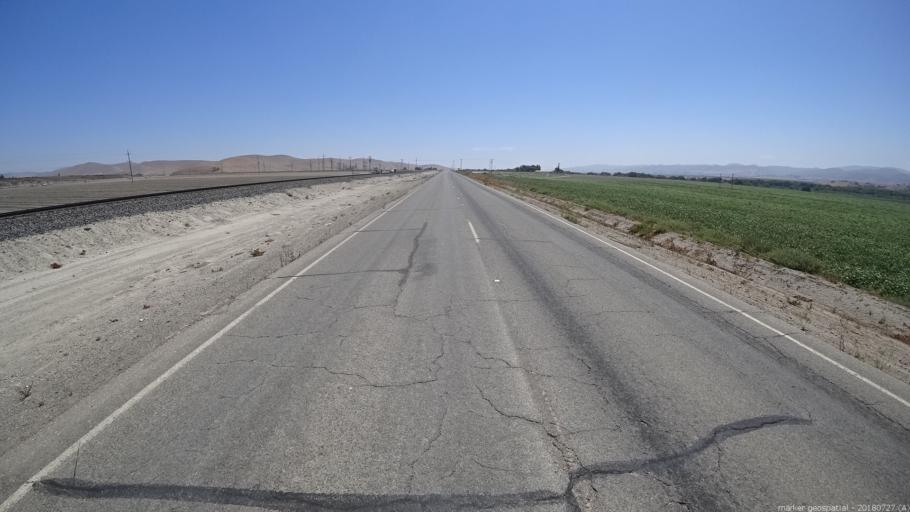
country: US
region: California
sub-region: Monterey County
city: King City
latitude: 36.0766
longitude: -120.9413
